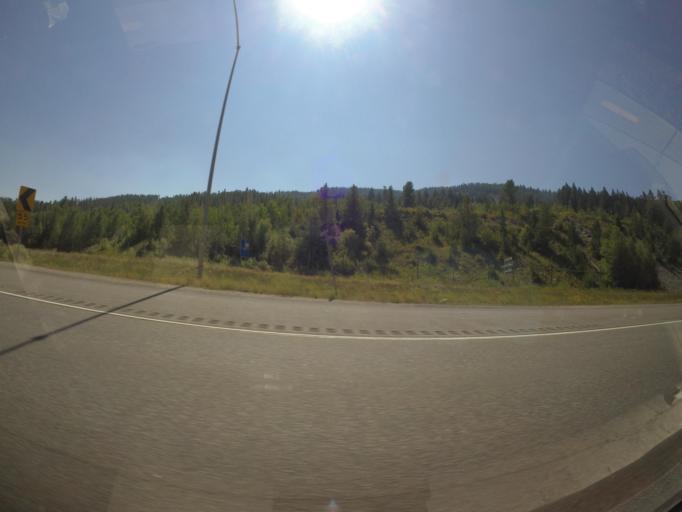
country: US
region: Colorado
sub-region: Eagle County
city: Minturn
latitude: 39.6078
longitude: -106.4546
